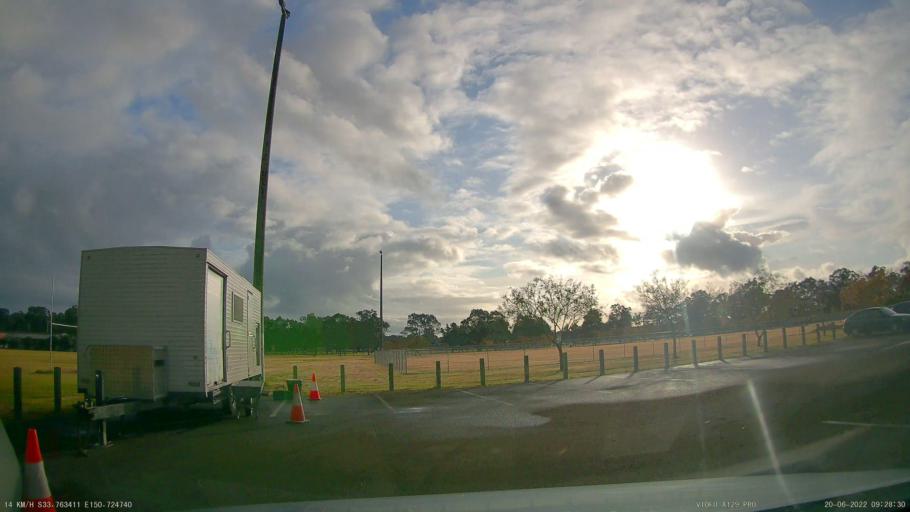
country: AU
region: New South Wales
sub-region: Penrith Municipality
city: Kingswood Park
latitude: -33.7632
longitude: 150.7246
